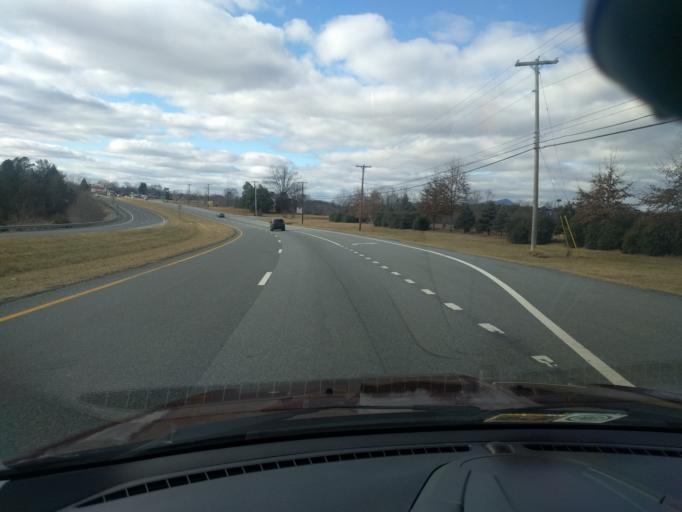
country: US
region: Virginia
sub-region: City of Bedford
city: Bedford
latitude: 37.3194
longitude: -79.4843
